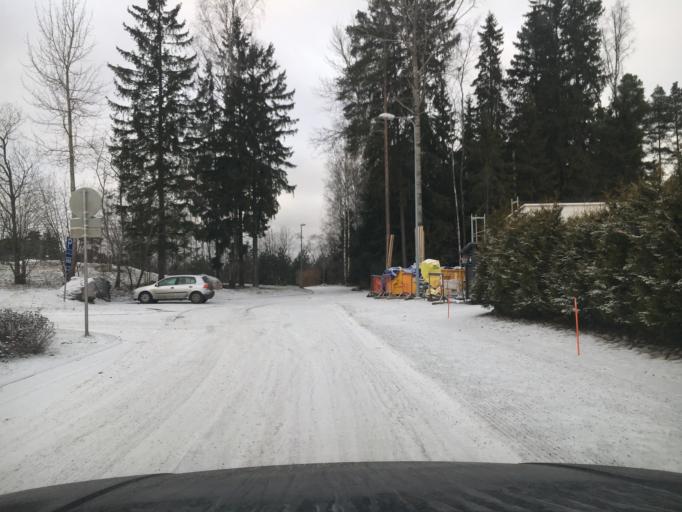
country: FI
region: Uusimaa
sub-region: Helsinki
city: Espoo
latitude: 60.1644
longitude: 24.6610
